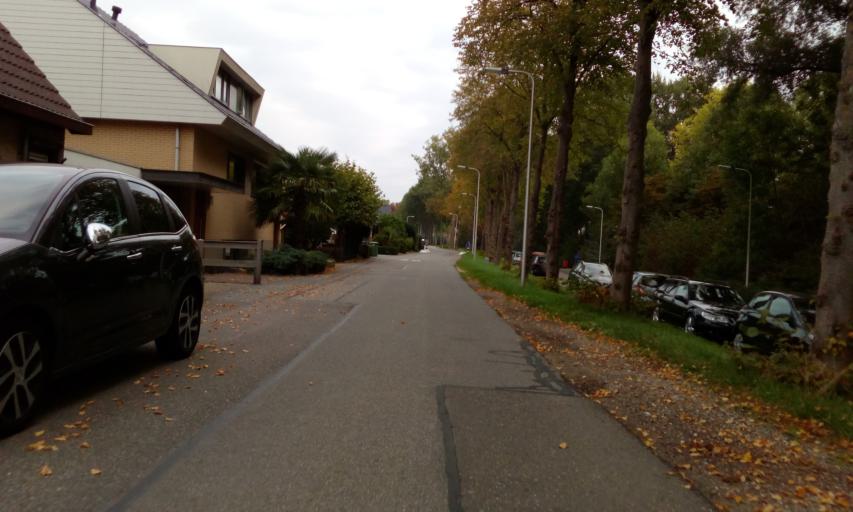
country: NL
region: South Holland
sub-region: Gemeente Albrandswaard
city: Rhoon
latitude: 51.8514
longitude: 4.4248
